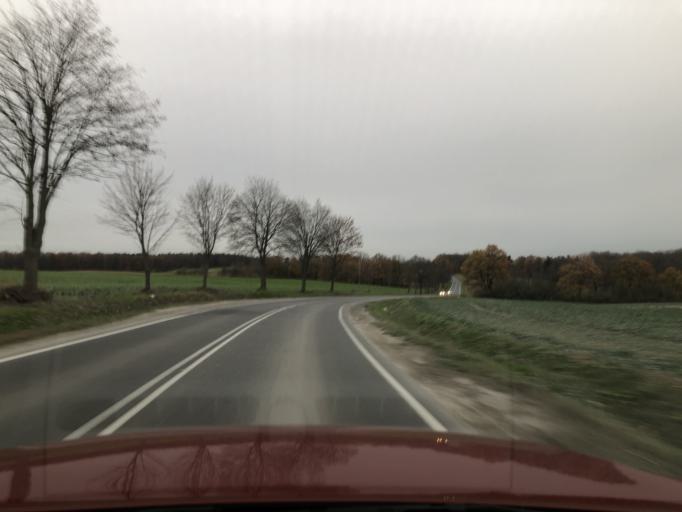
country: PL
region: Lower Silesian Voivodeship
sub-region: Powiat swidnicki
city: Zarow
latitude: 50.9669
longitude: 16.4966
